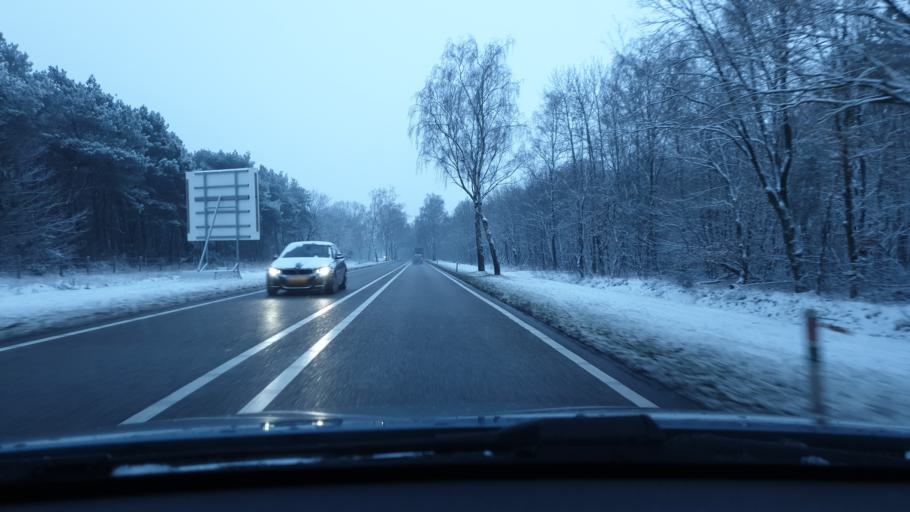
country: NL
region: North Brabant
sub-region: Gemeente Landerd
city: Reek
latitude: 51.7321
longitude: 5.6692
